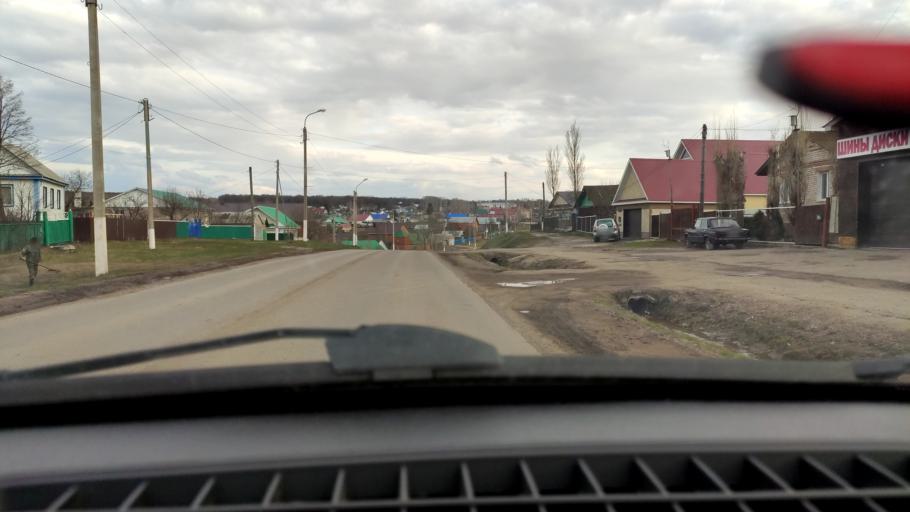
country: RU
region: Bashkortostan
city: Tolbazy
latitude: 54.0246
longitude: 55.8859
